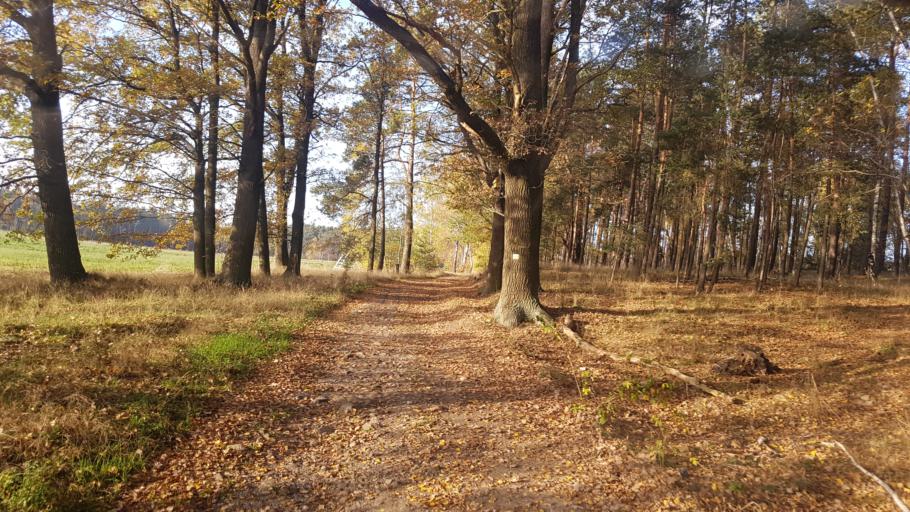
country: DE
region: Brandenburg
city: Calau
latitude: 51.6975
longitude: 13.9581
